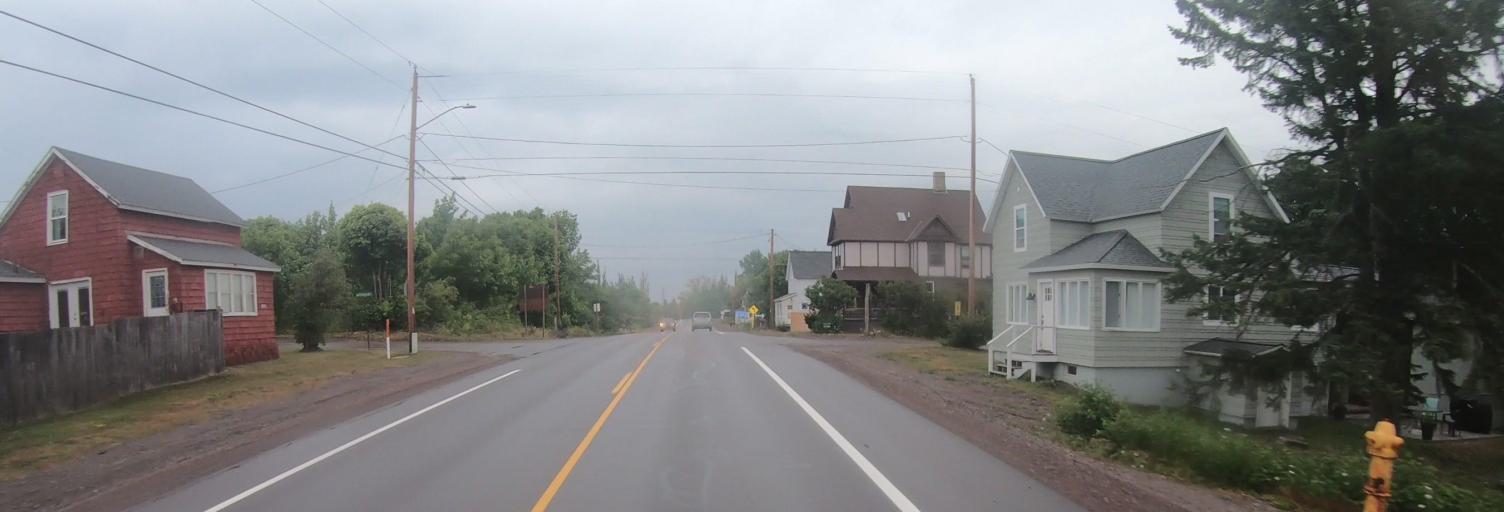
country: US
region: Michigan
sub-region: Houghton County
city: Laurium
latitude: 47.2581
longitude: -88.4292
